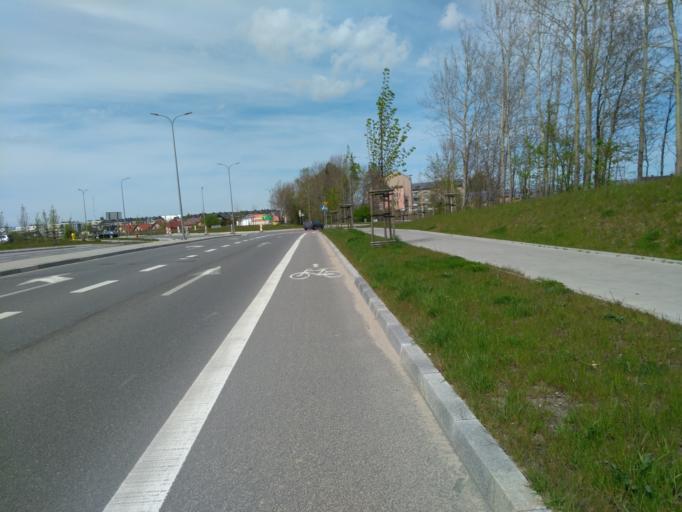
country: PL
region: Pomeranian Voivodeship
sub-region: Gdynia
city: Wielki Kack
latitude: 54.4155
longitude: 18.4801
